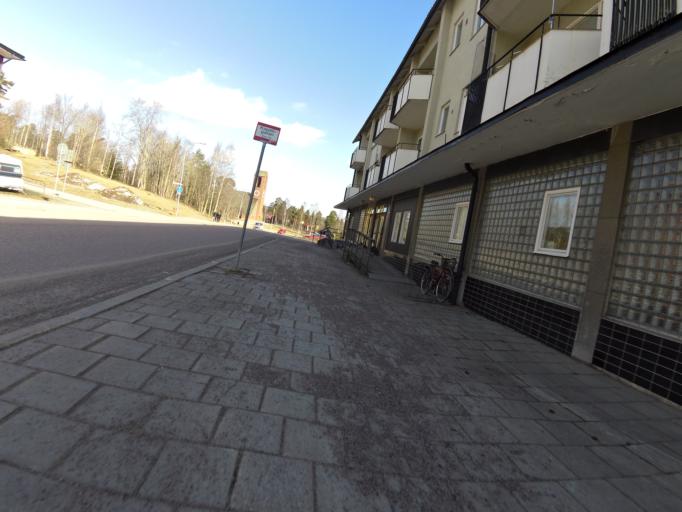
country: SE
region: Gaevleborg
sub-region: Hofors Kommun
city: Hofors
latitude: 60.5495
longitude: 16.2872
